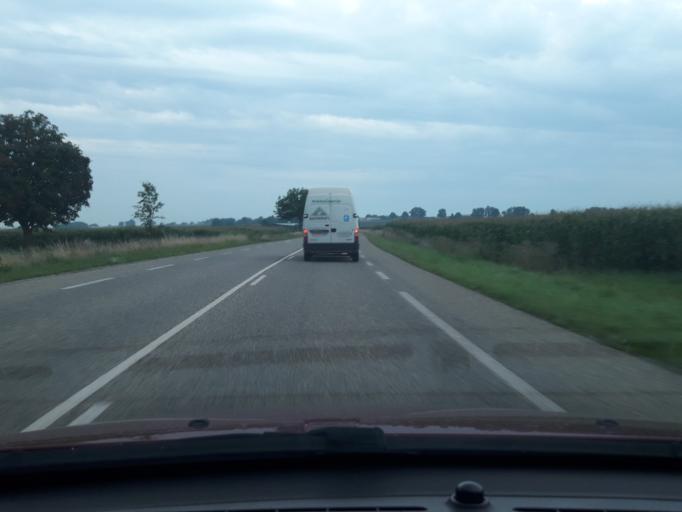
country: FR
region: Alsace
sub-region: Departement du Bas-Rhin
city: Dauendorf
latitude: 48.7922
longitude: 7.6642
